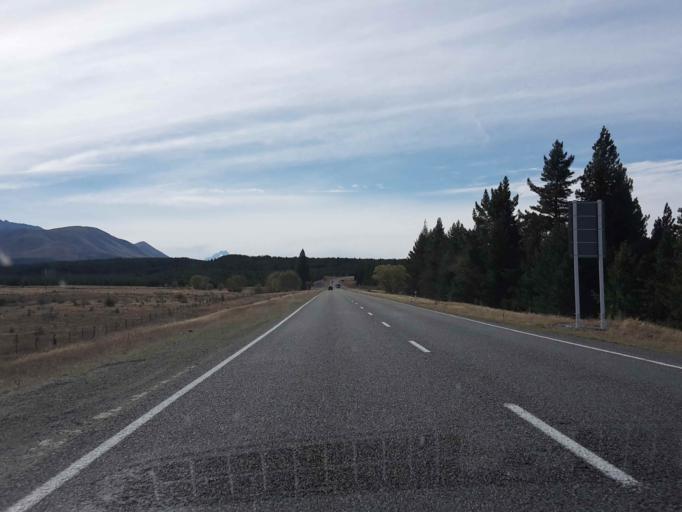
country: NZ
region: Canterbury
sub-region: Timaru District
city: Pleasant Point
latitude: -44.1986
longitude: 170.1203
